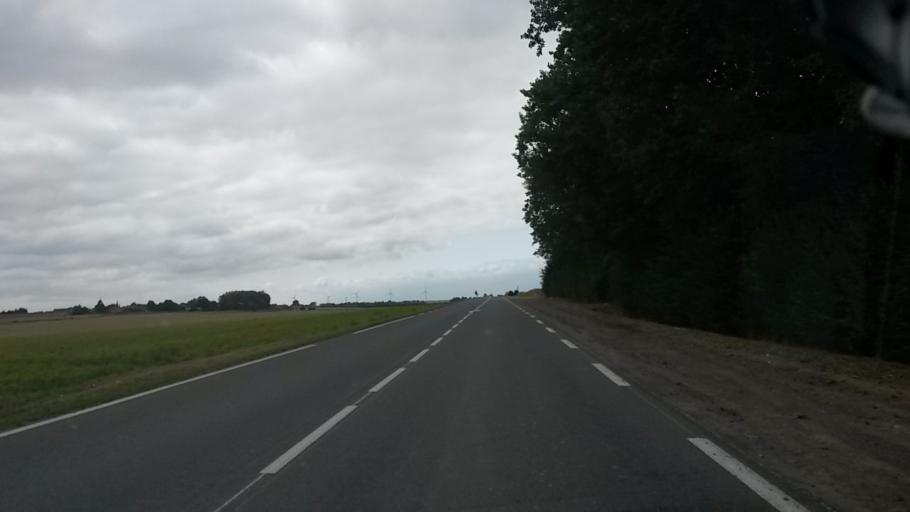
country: FR
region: Nord-Pas-de-Calais
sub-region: Departement du Nord
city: Fontaine-Notre-Dame
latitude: 50.1623
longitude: 3.1387
